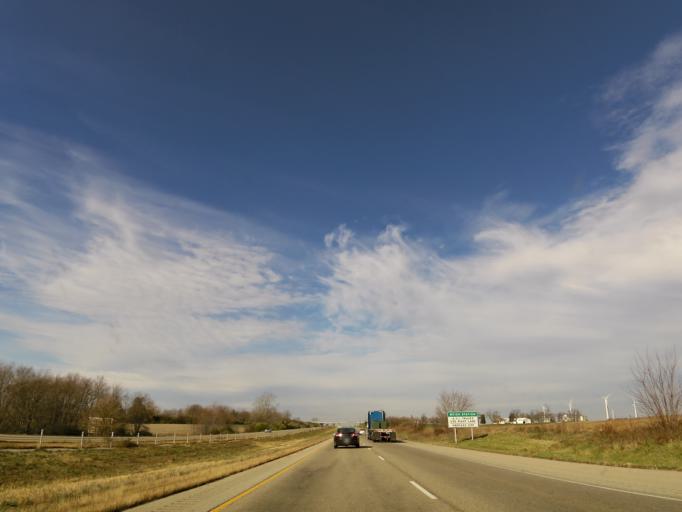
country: US
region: Illinois
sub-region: McLean County
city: Twin Grove
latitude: 40.5422
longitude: -89.0801
